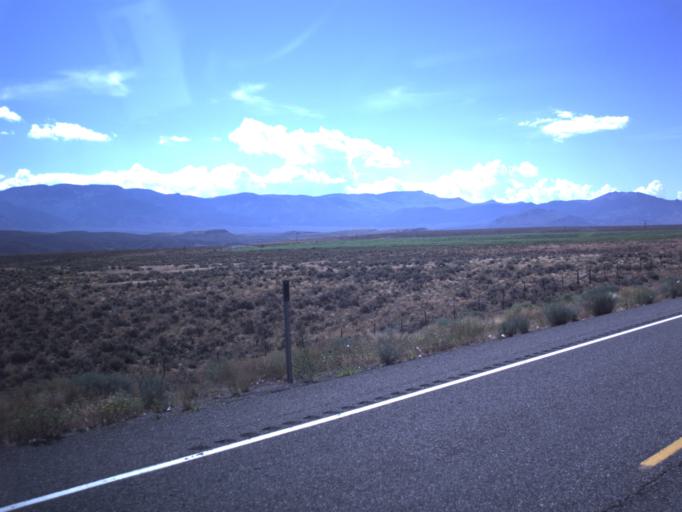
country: US
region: Utah
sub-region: Piute County
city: Junction
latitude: 38.4265
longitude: -112.2317
